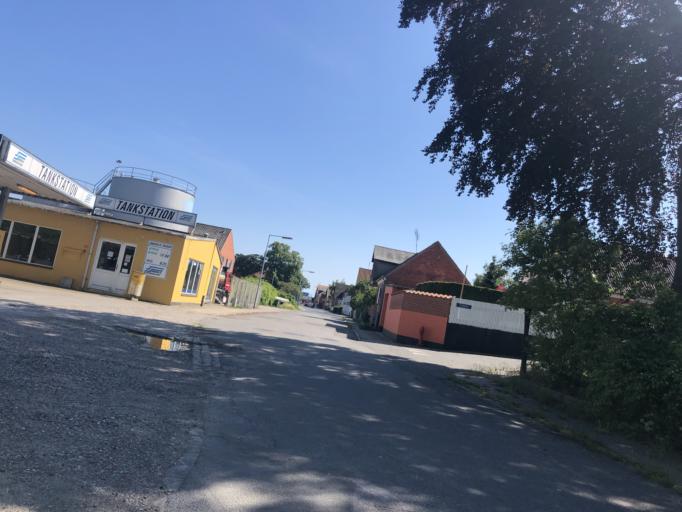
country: DK
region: South Denmark
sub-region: AEro Kommune
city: Marstal
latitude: 54.8568
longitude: 10.5202
